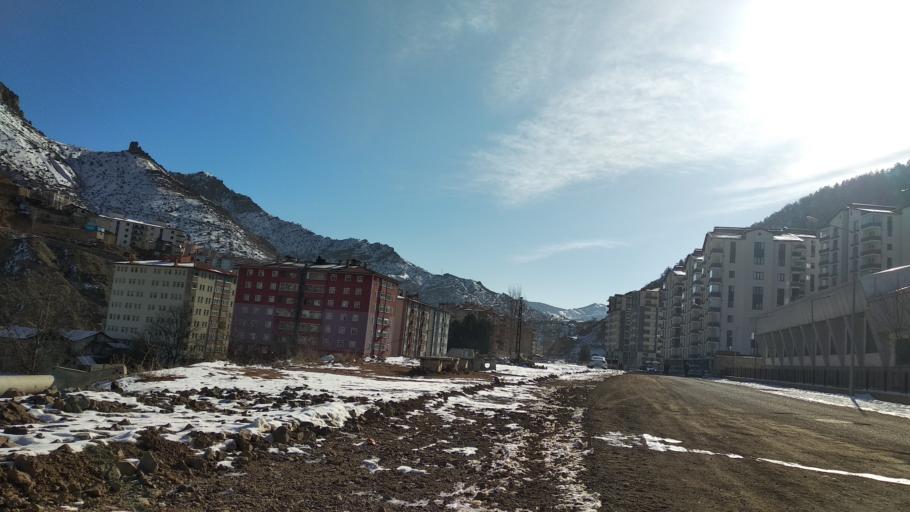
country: TR
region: Gumushane
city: Gumushkhane
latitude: 40.4527
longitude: 39.4912
